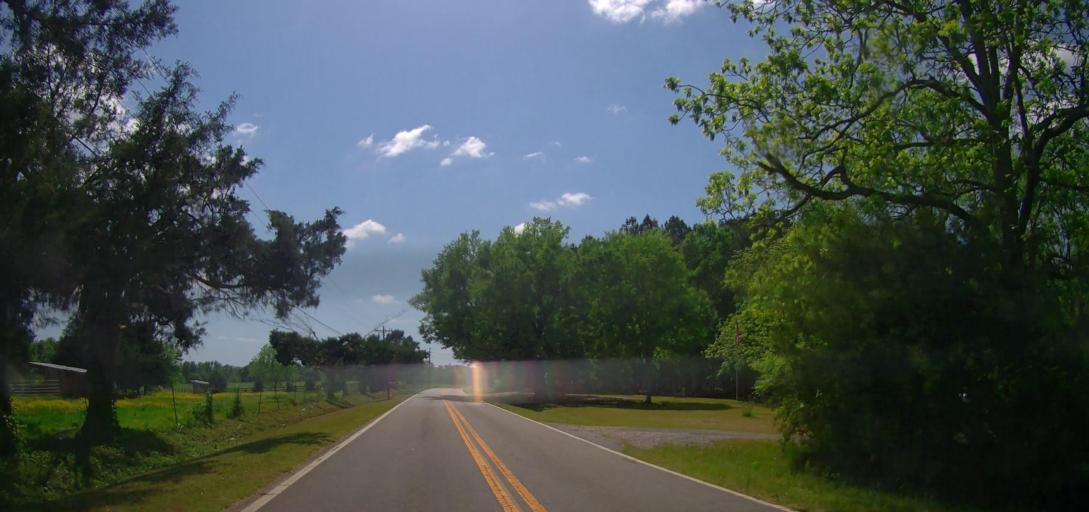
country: US
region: Georgia
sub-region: Putnam County
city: Eatonton
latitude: 33.3231
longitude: -83.3061
